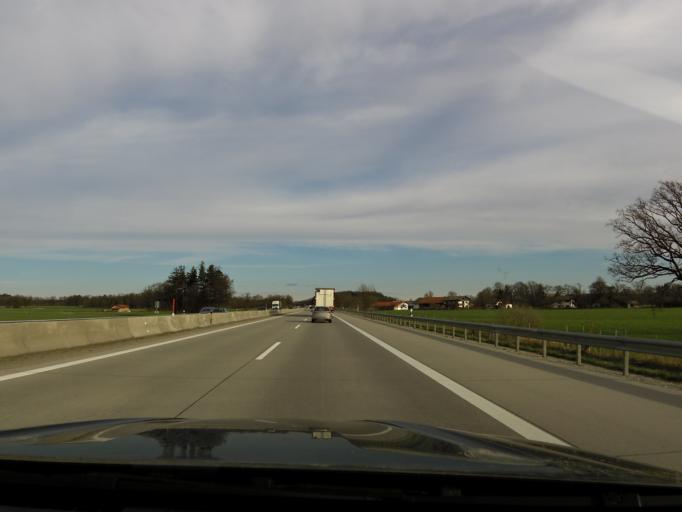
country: DE
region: Bavaria
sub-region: Upper Bavaria
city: Flintsbach
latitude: 47.7441
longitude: 12.1232
